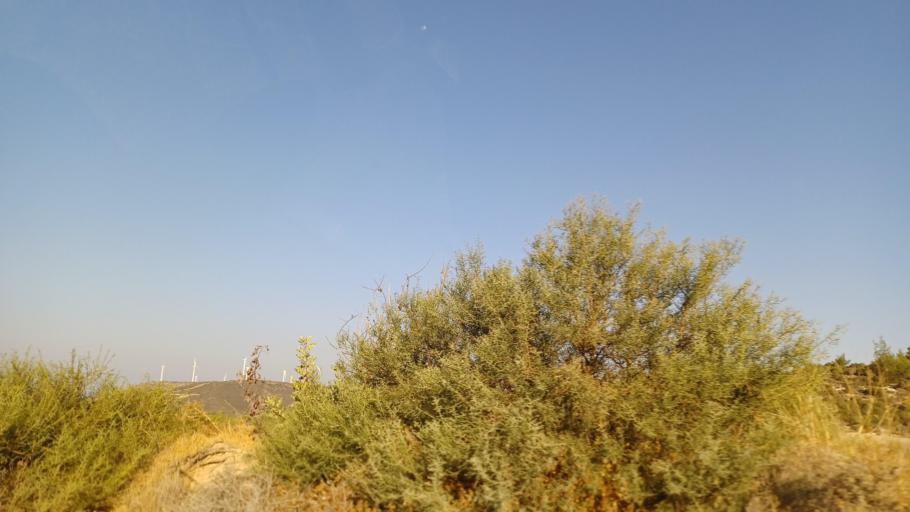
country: CY
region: Limassol
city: Pissouri
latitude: 34.7227
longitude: 32.6783
